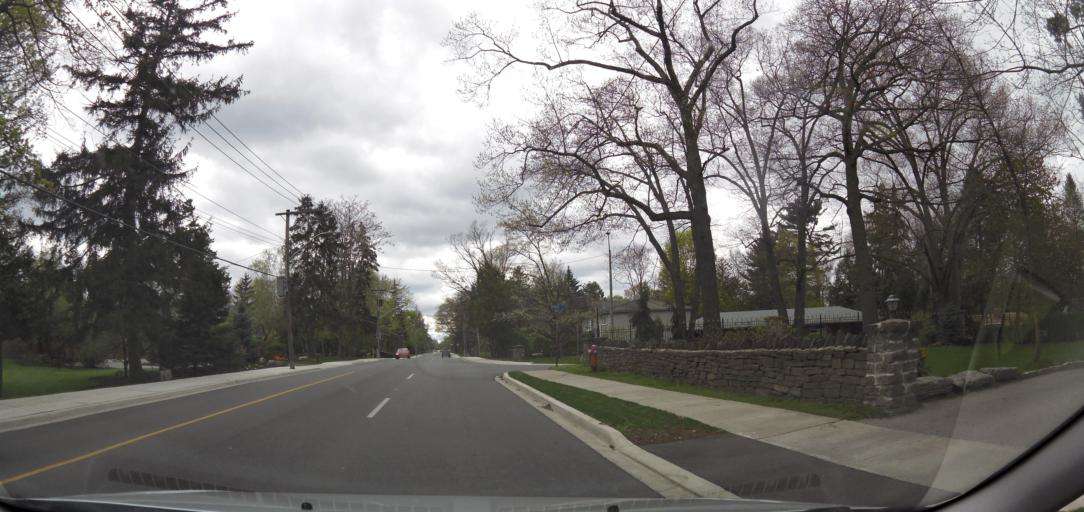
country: CA
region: Ontario
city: Mississauga
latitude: 43.5514
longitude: -79.6044
